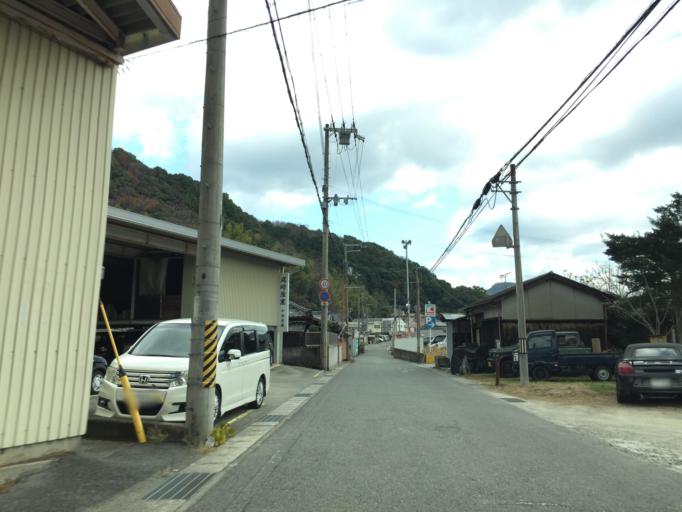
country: JP
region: Wakayama
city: Kainan
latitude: 34.1639
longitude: 135.2860
